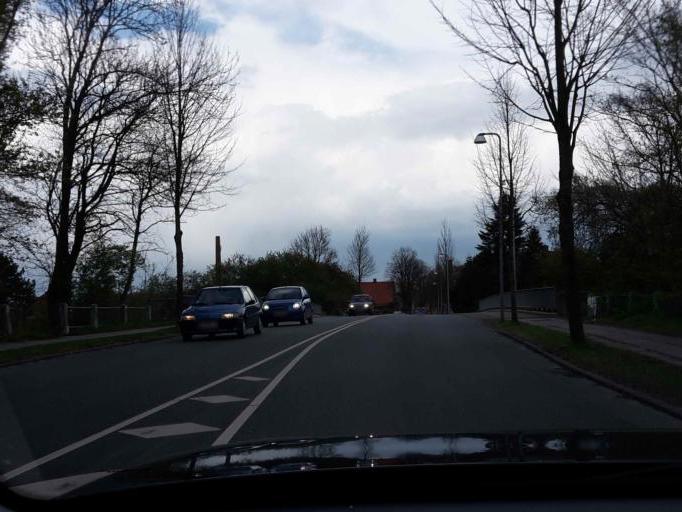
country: DK
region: South Denmark
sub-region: Odense Kommune
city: Odense
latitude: 55.3988
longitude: 10.3543
